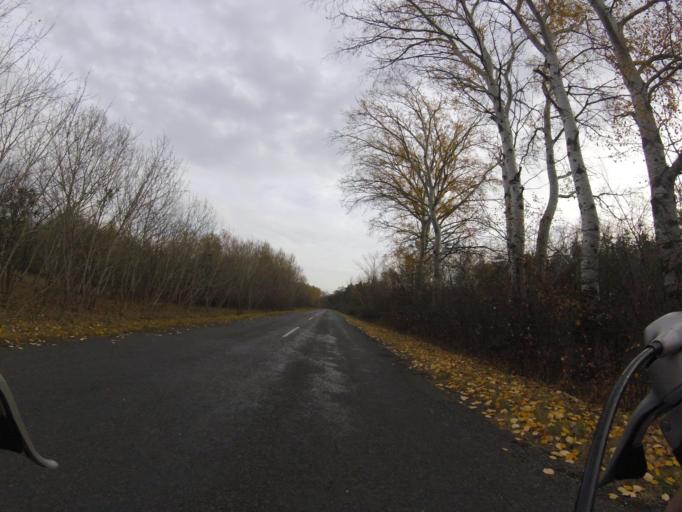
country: HU
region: Pest
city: Csemo
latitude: 47.0861
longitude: 19.6598
